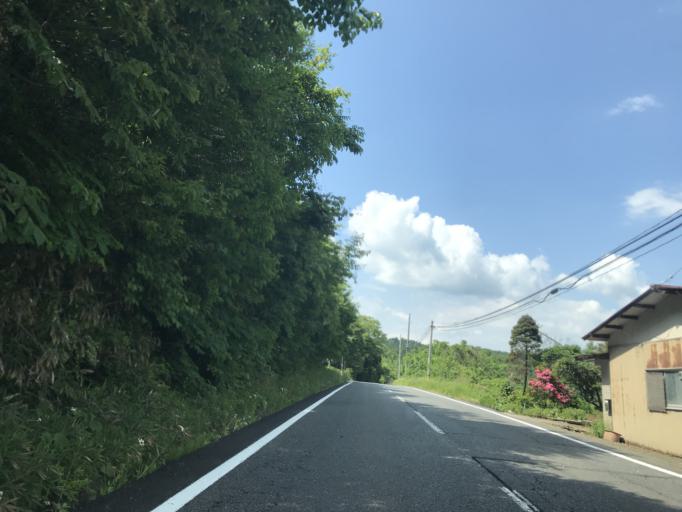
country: JP
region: Miyagi
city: Furukawa
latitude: 38.7267
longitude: 140.9524
